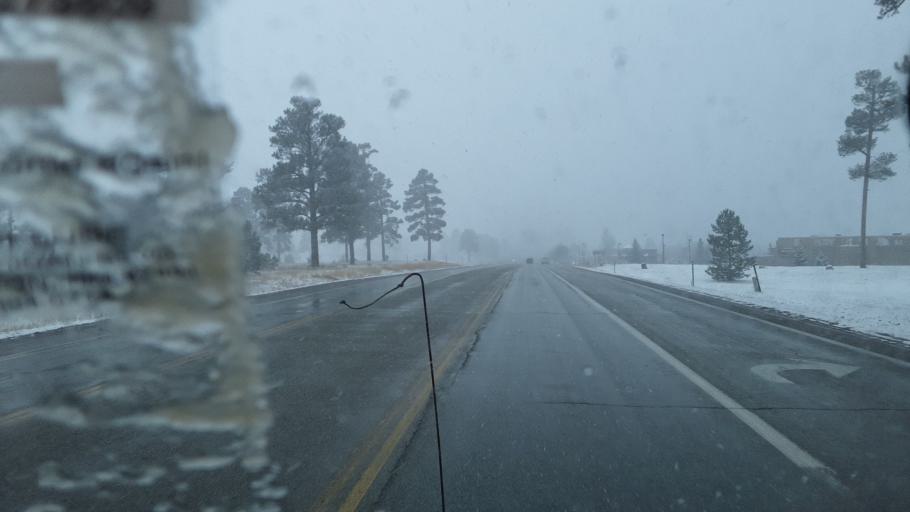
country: US
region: Colorado
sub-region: Archuleta County
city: Pagosa Springs
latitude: 37.2583
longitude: -107.0712
